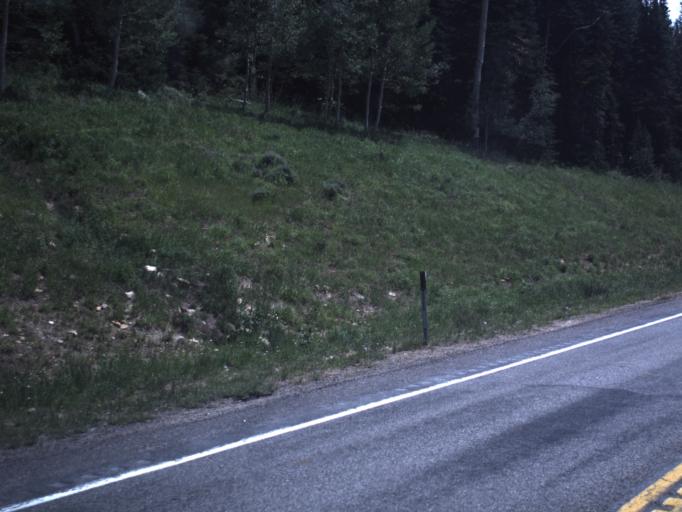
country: US
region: Utah
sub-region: Sanpete County
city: Fairview
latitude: 39.5912
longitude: -111.2643
